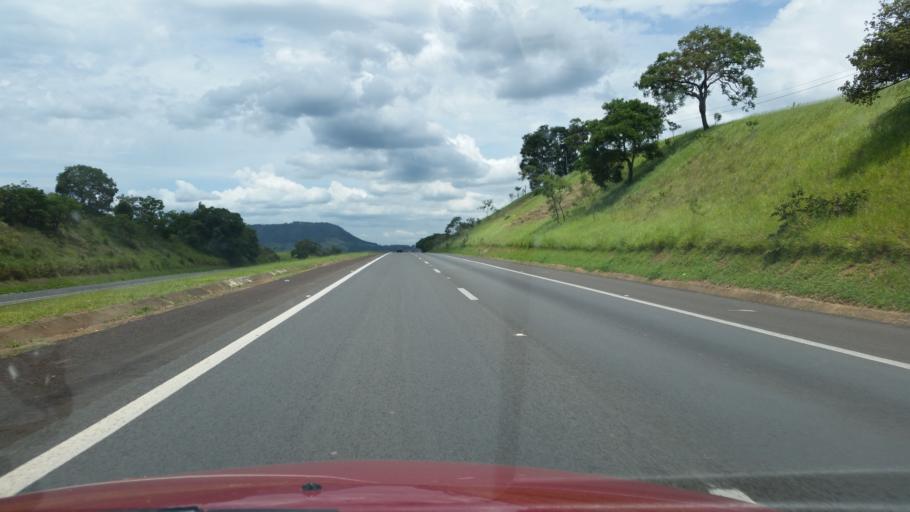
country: BR
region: Sao Paulo
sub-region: Itatinga
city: Itatinga
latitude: -23.1440
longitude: -48.4150
